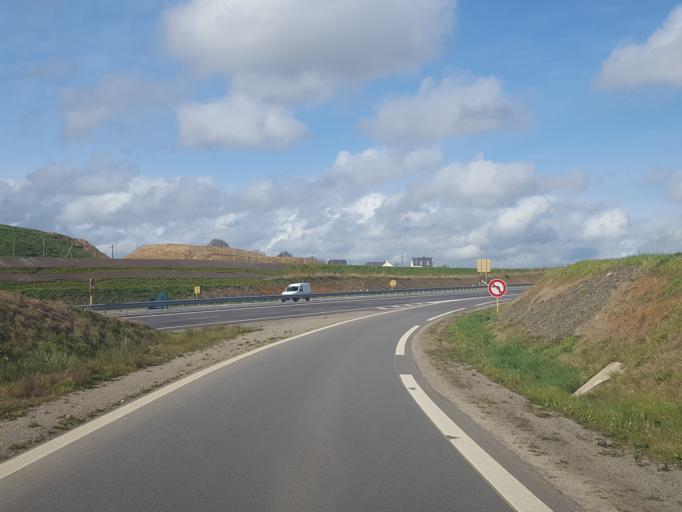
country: FR
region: Brittany
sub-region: Departement d'Ille-et-Vilaine
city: Guignen
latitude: 47.9223
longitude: -1.8510
